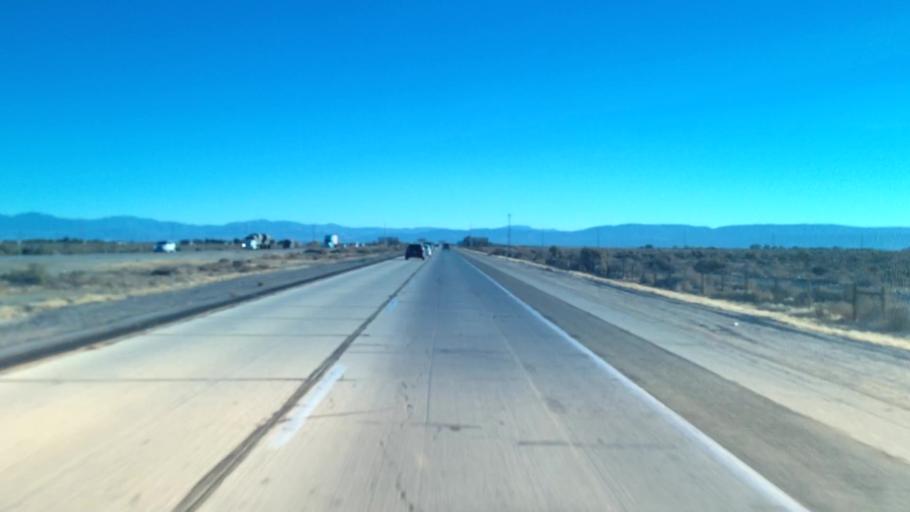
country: US
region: California
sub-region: Kern County
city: Rosamond
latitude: 34.8435
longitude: -118.1713
